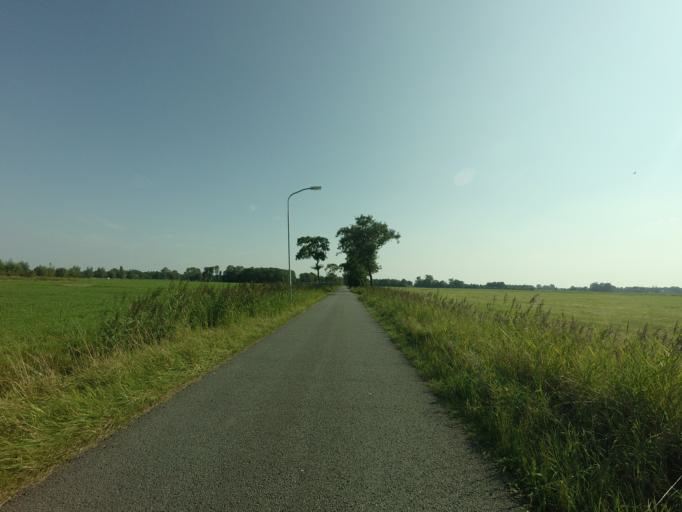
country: NL
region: Groningen
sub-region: Gemeente Zuidhorn
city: Zuidhorn
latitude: 53.2084
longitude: 6.4360
